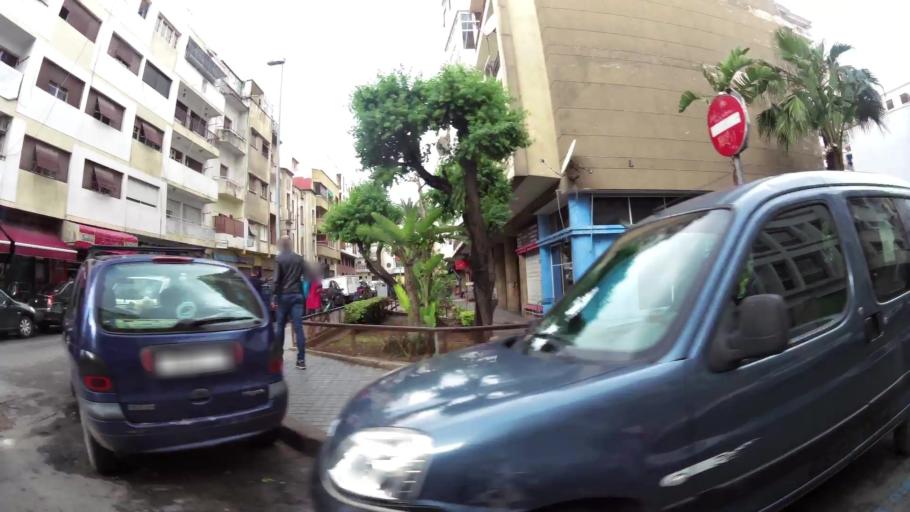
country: MA
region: Grand Casablanca
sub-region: Casablanca
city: Casablanca
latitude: 33.5848
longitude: -7.6186
